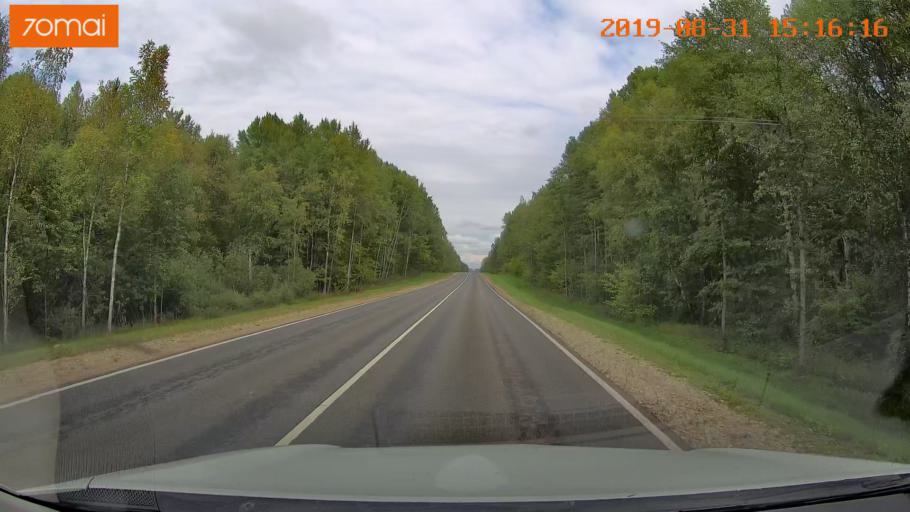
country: RU
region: Kaluga
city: Baryatino
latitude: 54.4584
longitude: 34.3461
